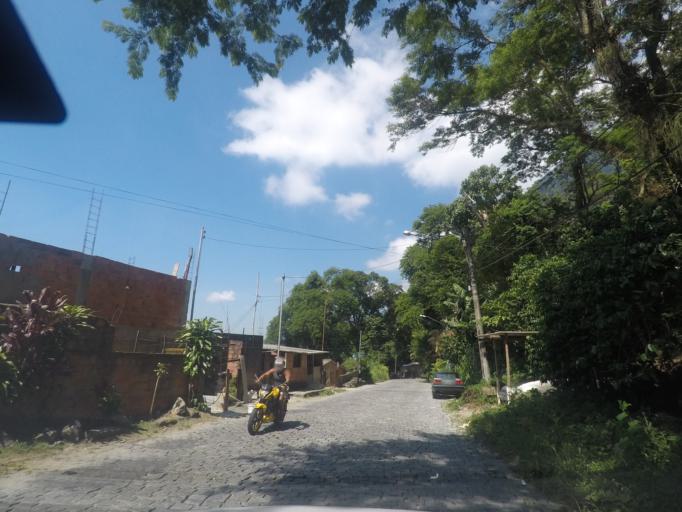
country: BR
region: Rio de Janeiro
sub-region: Petropolis
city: Petropolis
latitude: -22.5477
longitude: -43.1795
